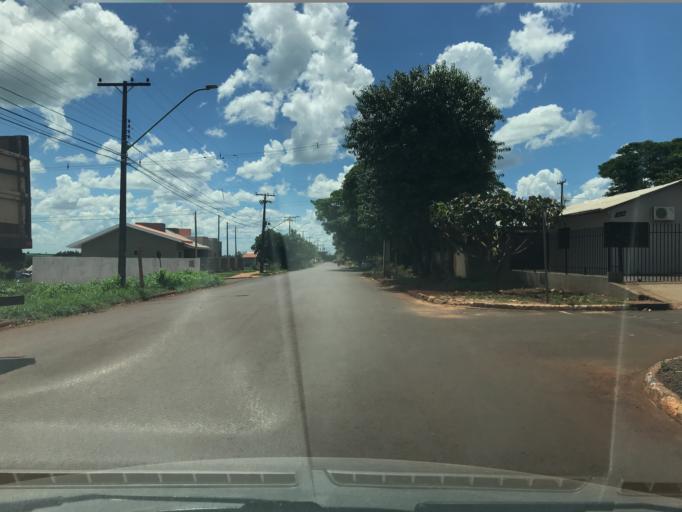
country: BR
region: Parana
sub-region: Palotina
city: Palotina
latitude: -24.2728
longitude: -53.8485
